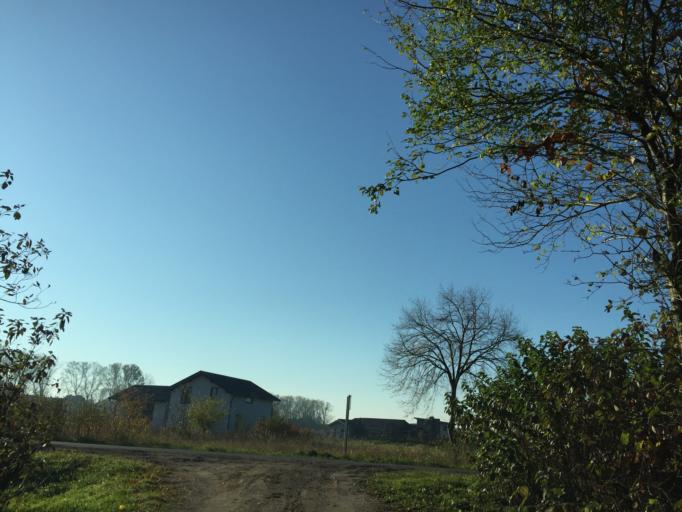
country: LT
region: Klaipedos apskritis
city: Kretinga
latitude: 55.8930
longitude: 21.2092
